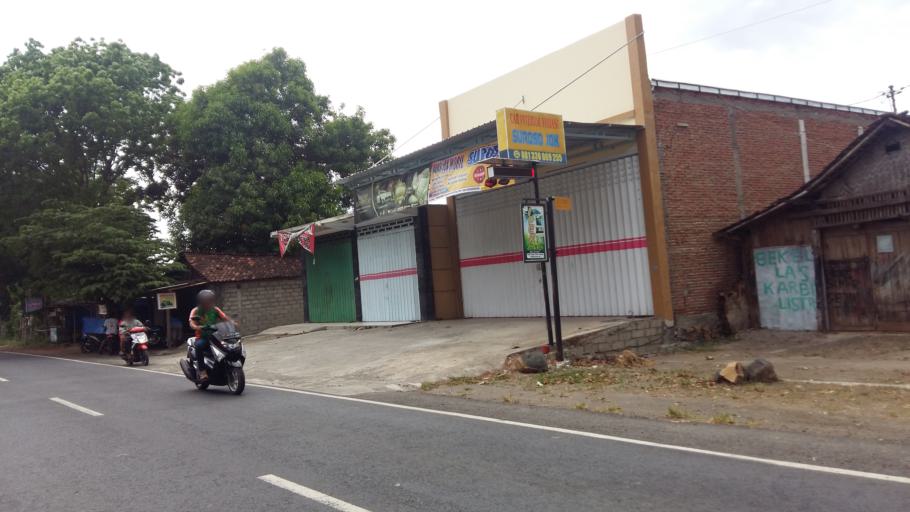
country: ID
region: East Java
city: Krajan
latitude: -8.3196
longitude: 114.2848
